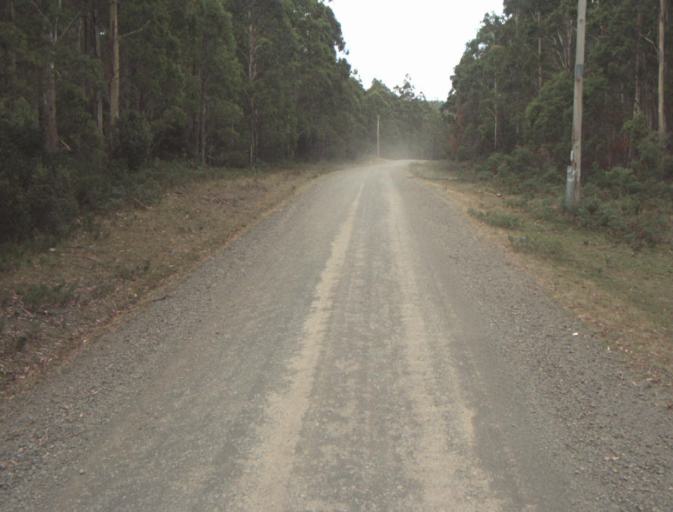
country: AU
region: Tasmania
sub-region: Dorset
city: Scottsdale
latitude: -41.4404
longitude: 147.5156
